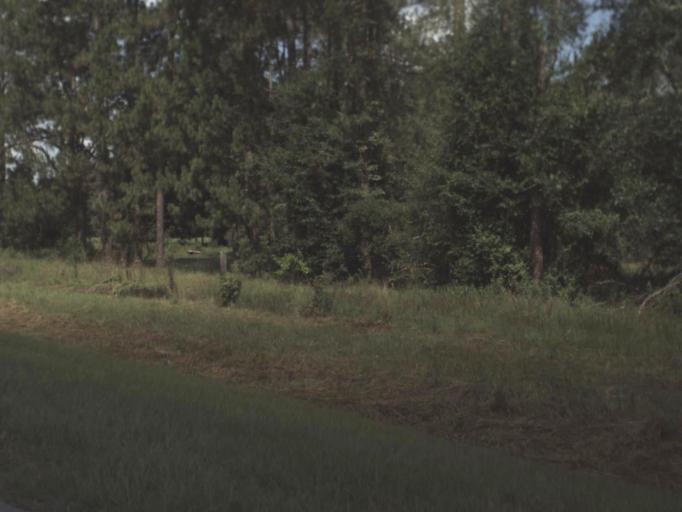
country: US
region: Florida
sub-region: Baker County
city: Macclenny
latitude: 30.1715
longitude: -82.1800
